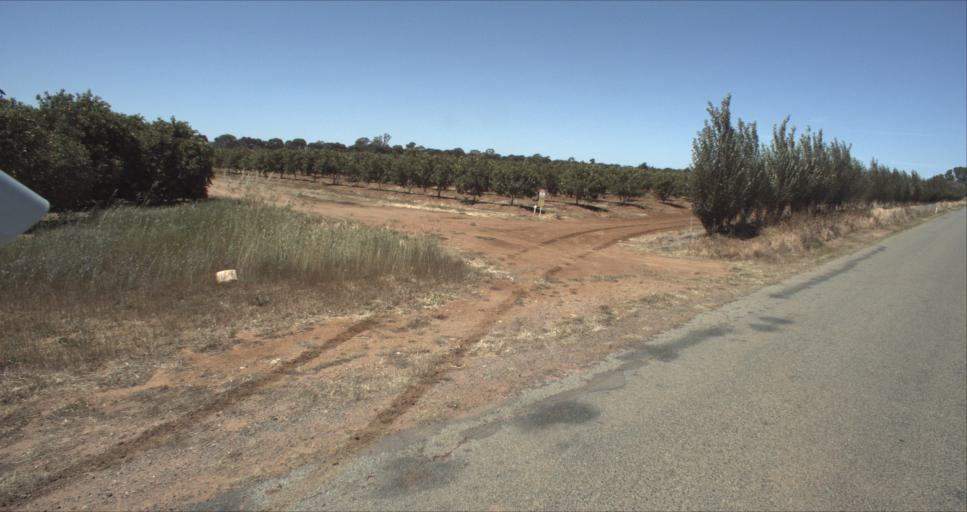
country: AU
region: New South Wales
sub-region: Leeton
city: Leeton
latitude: -34.5447
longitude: 146.3671
